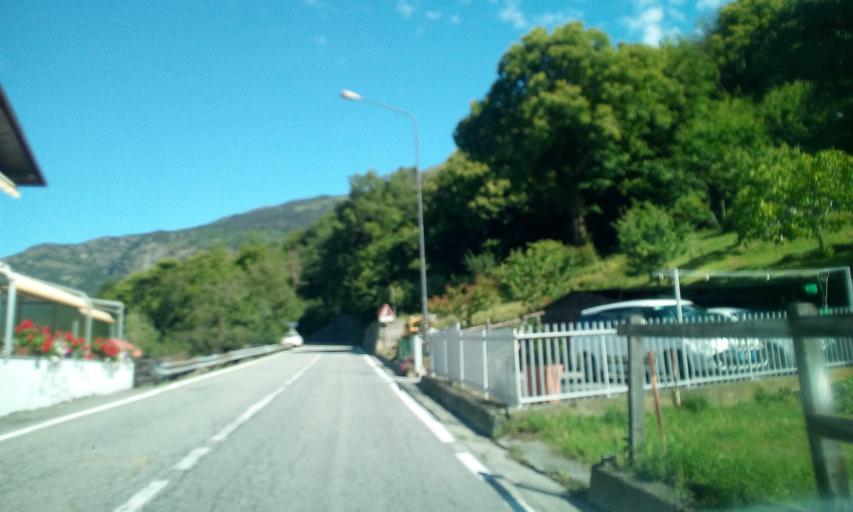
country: IT
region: Aosta Valley
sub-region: Valle d'Aosta
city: Saint-Vincent
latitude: 45.7530
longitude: 7.6660
